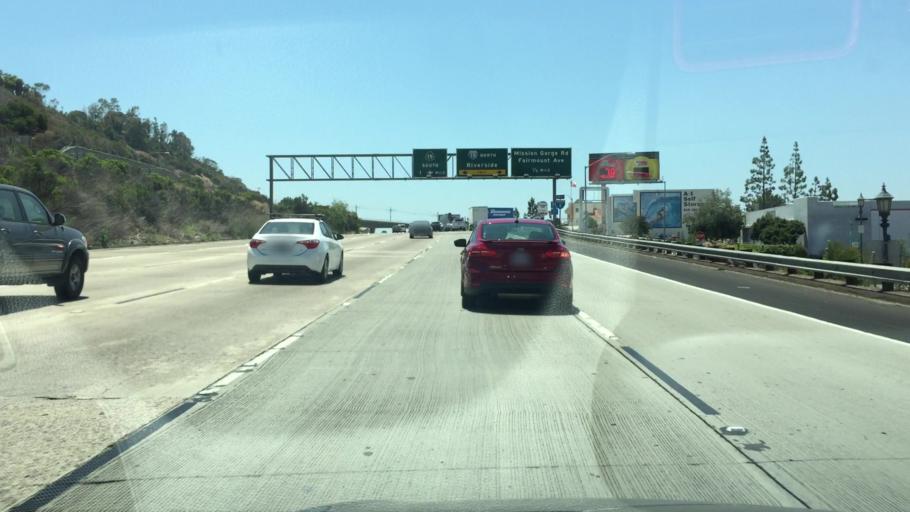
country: US
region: California
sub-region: San Diego County
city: La Mesa
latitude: 32.7809
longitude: -117.0910
